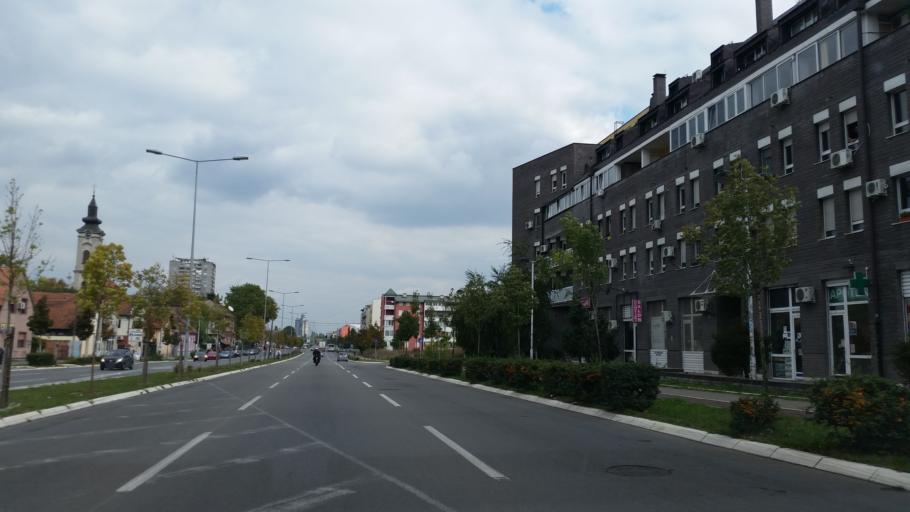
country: RS
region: Central Serbia
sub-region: Belgrade
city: Zemun
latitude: 44.8063
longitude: 20.3727
